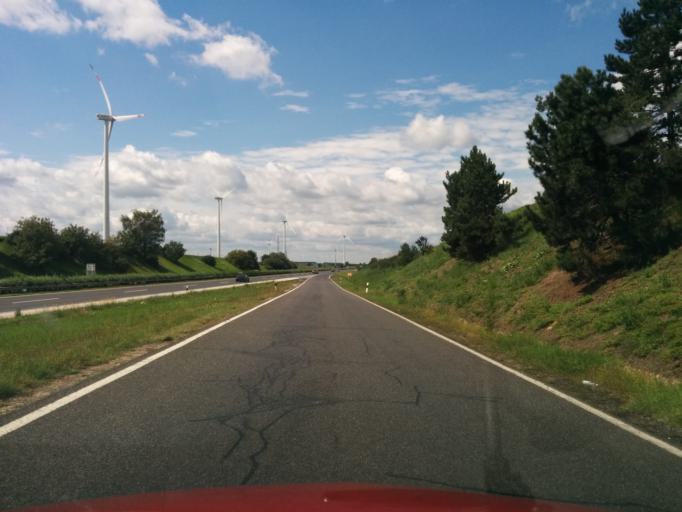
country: HU
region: Komarom-Esztergom
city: Nagyigmand
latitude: 47.6750
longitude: 18.0896
